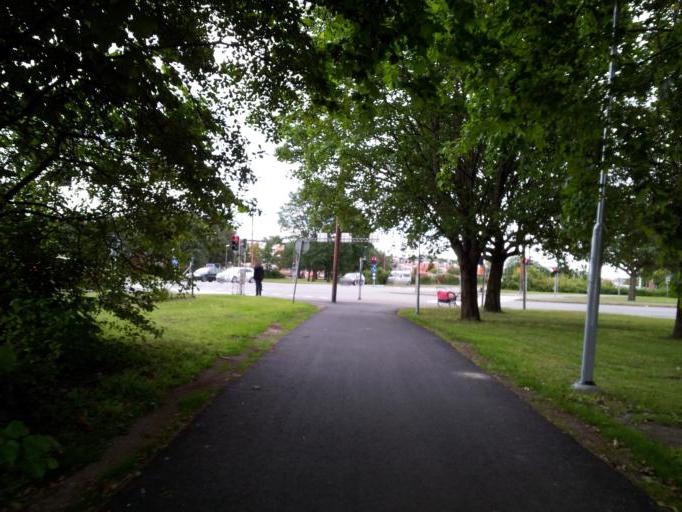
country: SE
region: Uppsala
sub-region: Uppsala Kommun
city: Uppsala
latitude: 59.8724
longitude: 17.6497
